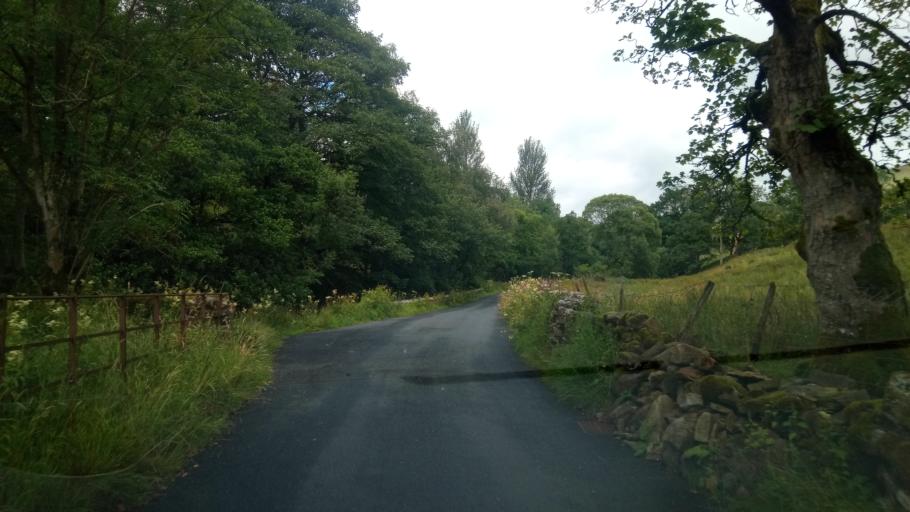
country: GB
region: England
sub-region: North Yorkshire
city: Ingleton
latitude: 54.2591
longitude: -2.3470
